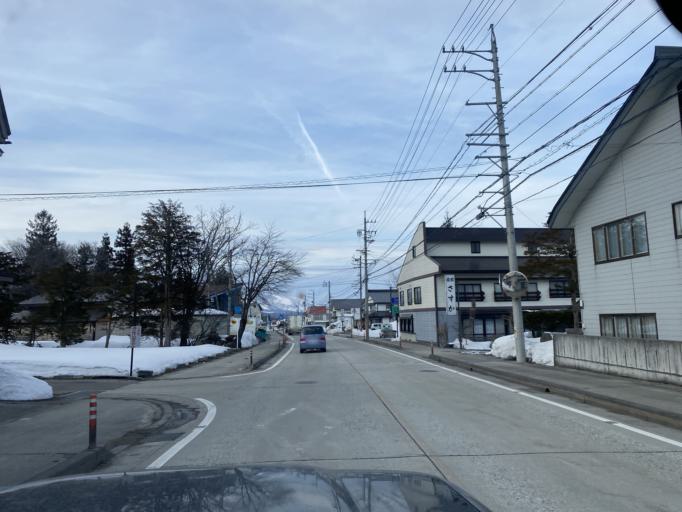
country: JP
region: Nagano
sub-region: Kitaazumi Gun
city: Hakuba
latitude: 36.6588
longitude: 137.8483
